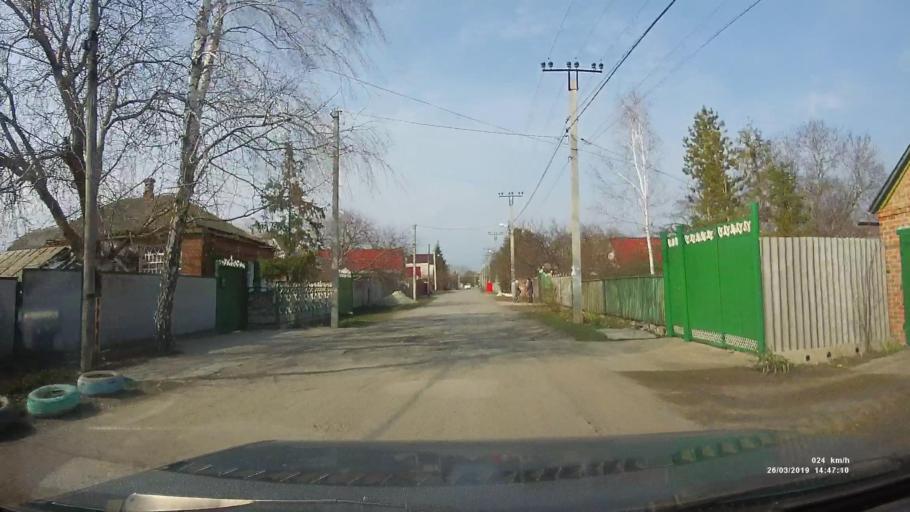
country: RU
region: Rostov
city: Novobessergenovka
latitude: 47.1897
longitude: 38.8594
